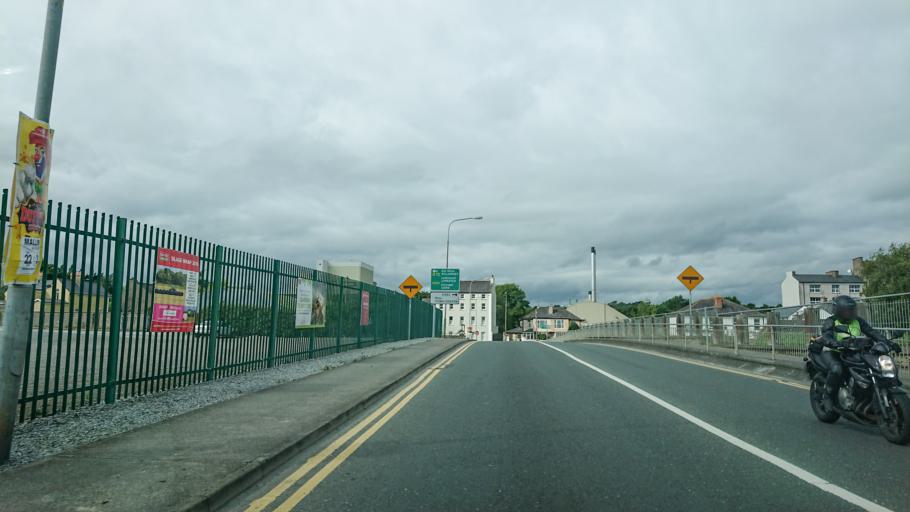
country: IE
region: Munster
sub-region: County Cork
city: Mallow
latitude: 52.1366
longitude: -8.6502
